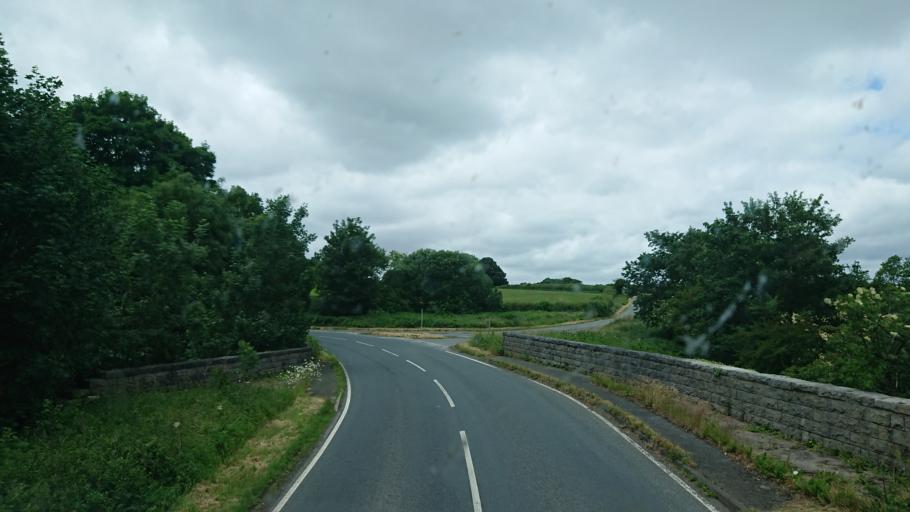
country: GB
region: England
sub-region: Cumbria
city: Milnthorpe
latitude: 54.2403
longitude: -2.7378
